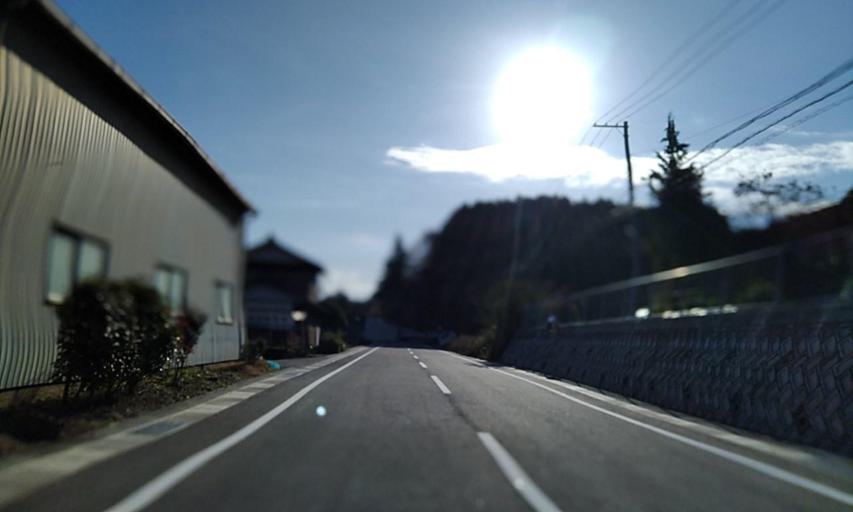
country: JP
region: Wakayama
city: Iwade
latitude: 34.1557
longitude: 135.3027
